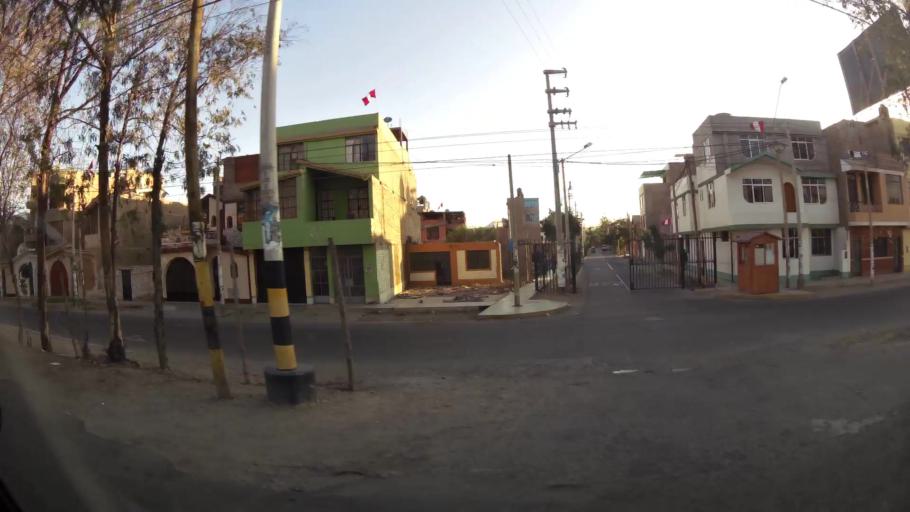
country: PE
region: Ica
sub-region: Provincia de Ica
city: Ica
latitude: -14.0797
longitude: -75.7377
